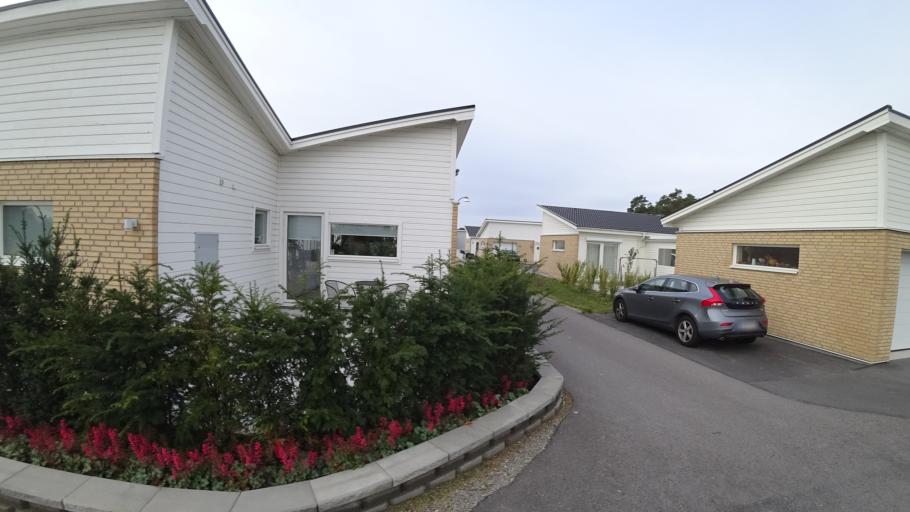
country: SE
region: Skane
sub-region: Kavlinge Kommun
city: Hofterup
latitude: 55.7933
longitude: 12.9752
